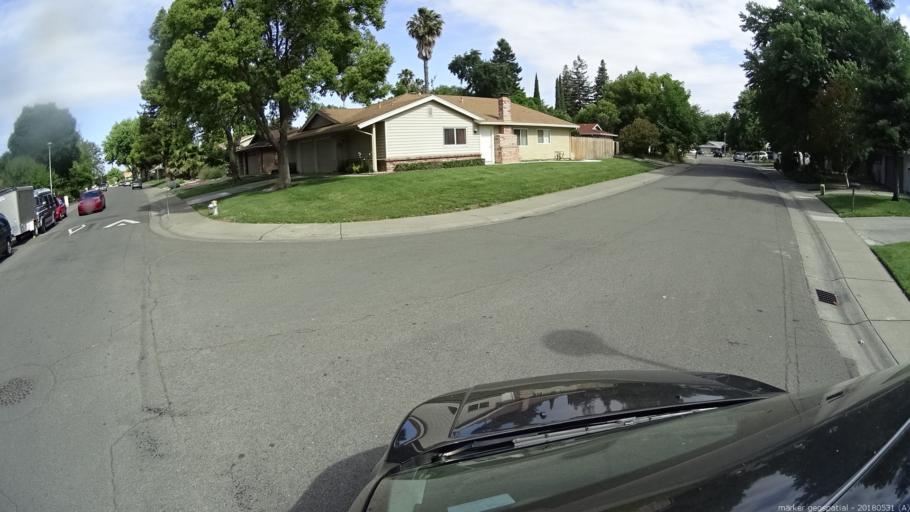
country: US
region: California
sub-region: Sacramento County
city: Sacramento
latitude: 38.6188
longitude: -121.4949
